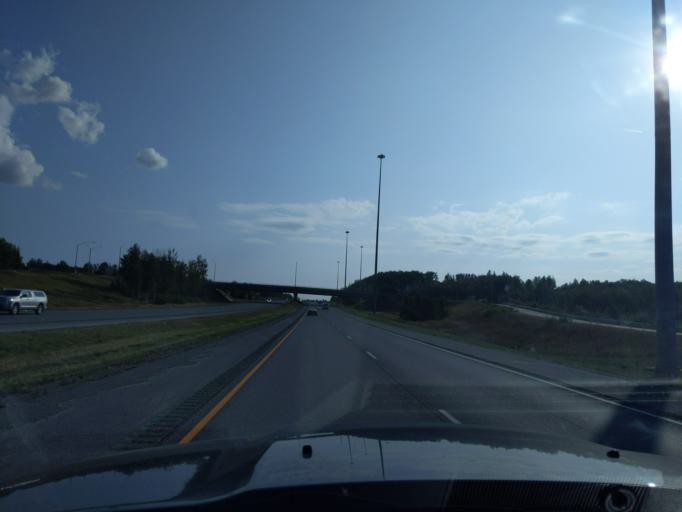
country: US
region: Alaska
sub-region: Anchorage Municipality
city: Eagle River
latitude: 61.3440
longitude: -149.5621
